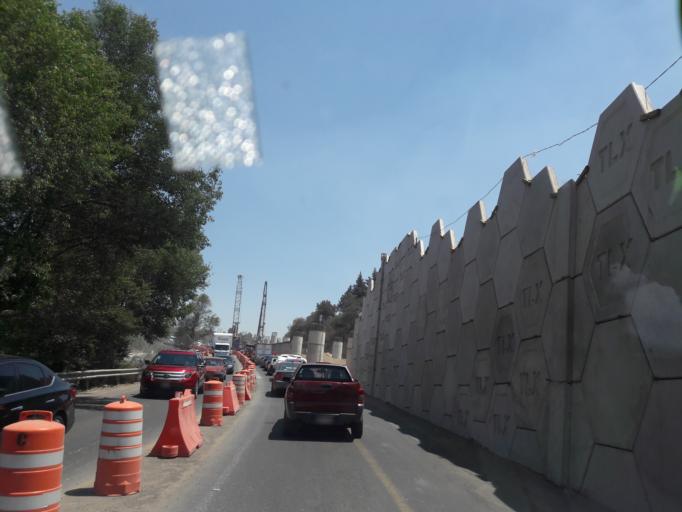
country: MX
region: Tlaxcala
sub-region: Apetatitlan de Antonio Carvajal
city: Belen Atzitzimititlan
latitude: 19.3438
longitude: -98.1993
